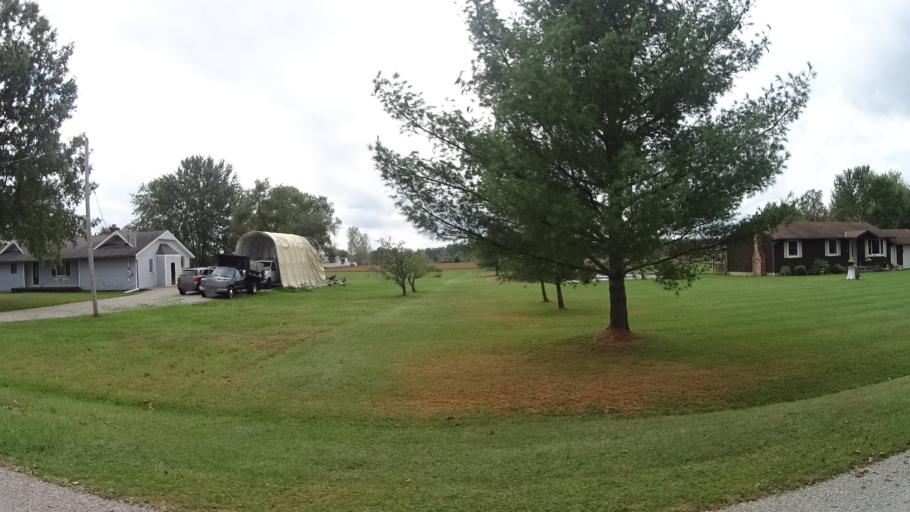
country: US
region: Ohio
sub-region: Lorain County
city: Grafton
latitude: 41.2563
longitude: -82.0246
